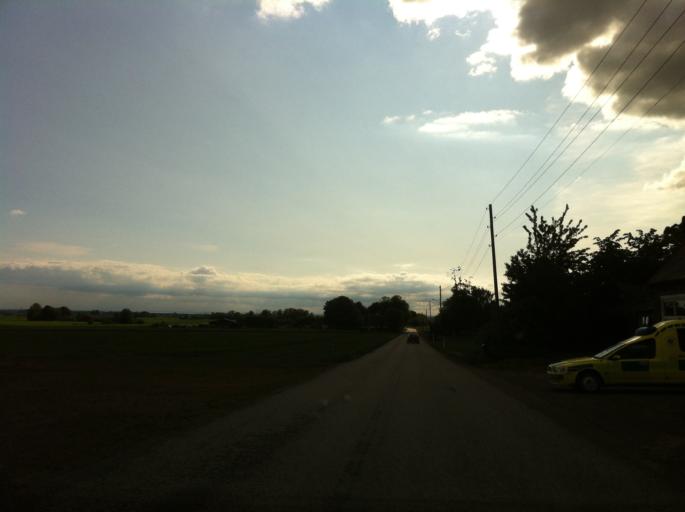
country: SE
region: Skane
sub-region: Svalovs Kommun
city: Kagerod
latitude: 55.9937
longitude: 13.0855
